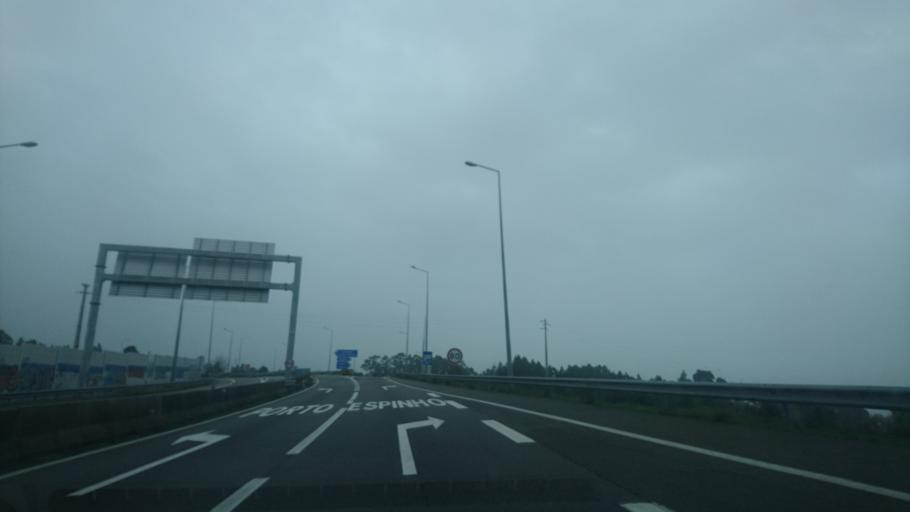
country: PT
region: Porto
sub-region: Vila Nova de Gaia
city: Gulpilhares
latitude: 41.0827
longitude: -8.6313
